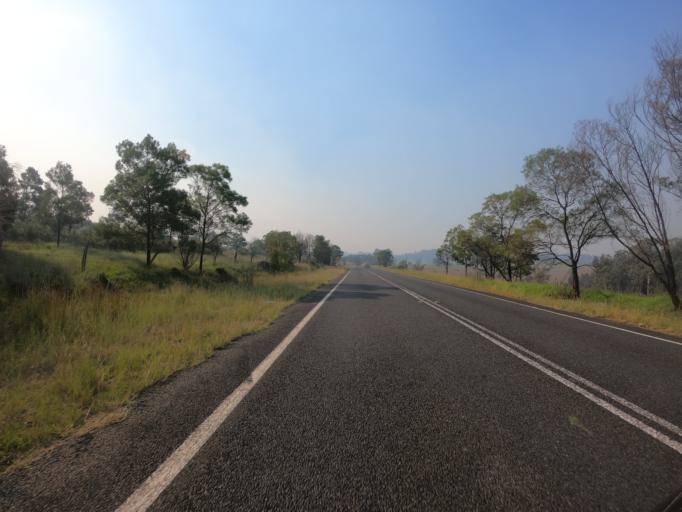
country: AU
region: New South Wales
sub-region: Wollondilly
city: Douglas Park
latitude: -34.2240
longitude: 150.7527
